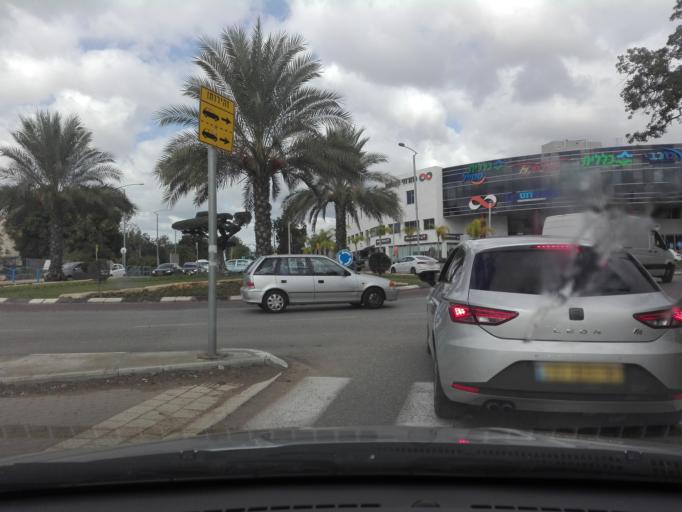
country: IL
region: Haifa
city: Hadera
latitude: 32.4757
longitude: 34.9766
